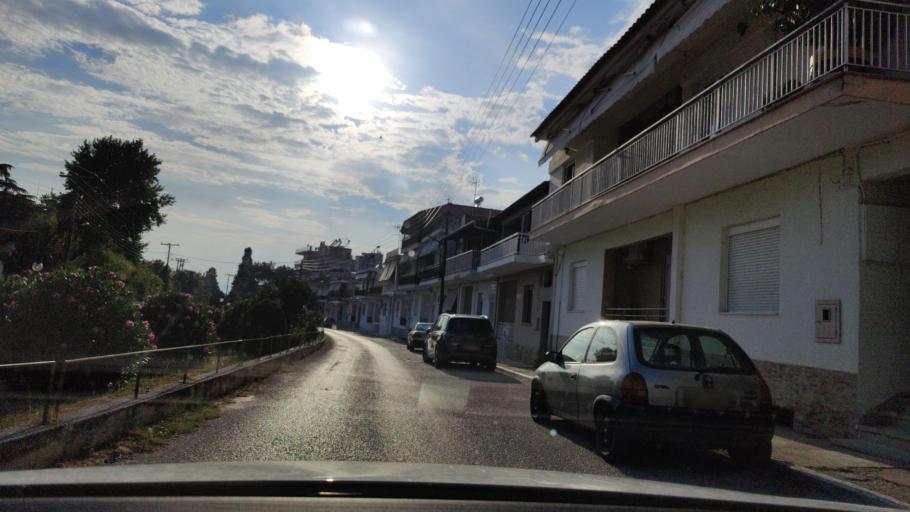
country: GR
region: Central Macedonia
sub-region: Nomos Serron
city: Sidirokastro
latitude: 41.2352
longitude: 23.3919
